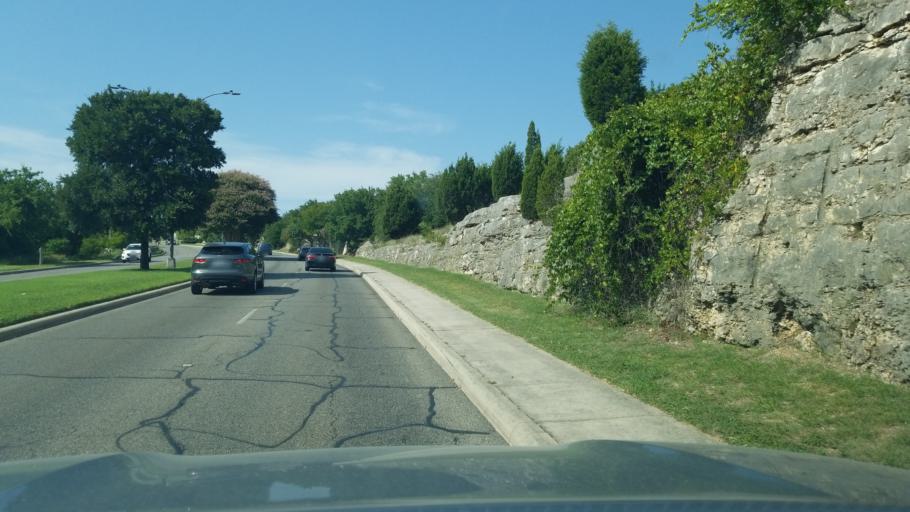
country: US
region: Texas
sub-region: Bexar County
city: Hollywood Park
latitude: 29.6510
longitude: -98.4808
